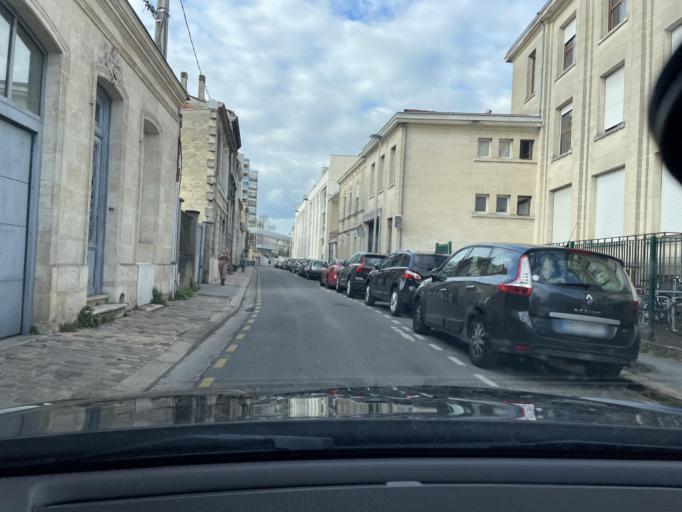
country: FR
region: Aquitaine
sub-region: Departement de la Gironde
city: Bordeaux
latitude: 44.8428
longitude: -0.5947
